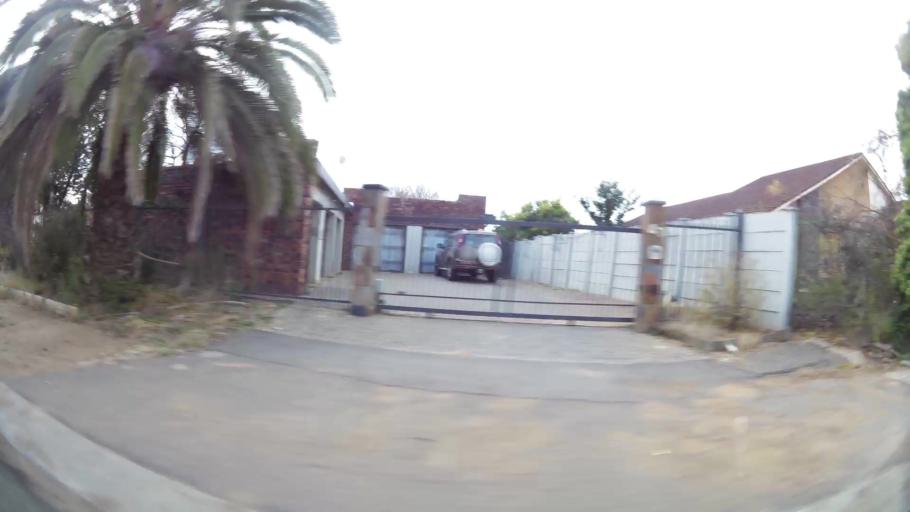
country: ZA
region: Orange Free State
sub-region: Mangaung Metropolitan Municipality
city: Bloemfontein
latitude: -29.1201
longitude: 26.1647
